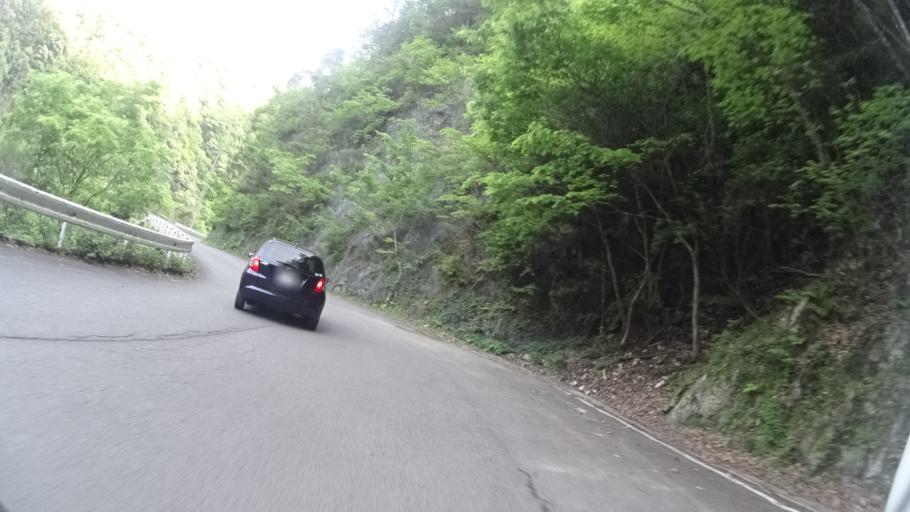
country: JP
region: Tokushima
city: Ikedacho
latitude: 33.9417
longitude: 133.8128
